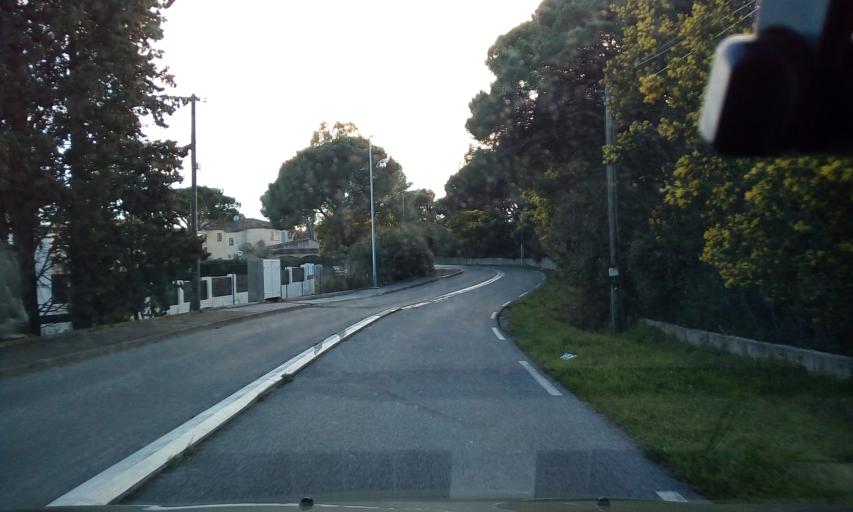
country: FR
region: Provence-Alpes-Cote d'Azur
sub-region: Departement du Var
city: Saint-Raphael
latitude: 43.4396
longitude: 6.7673
